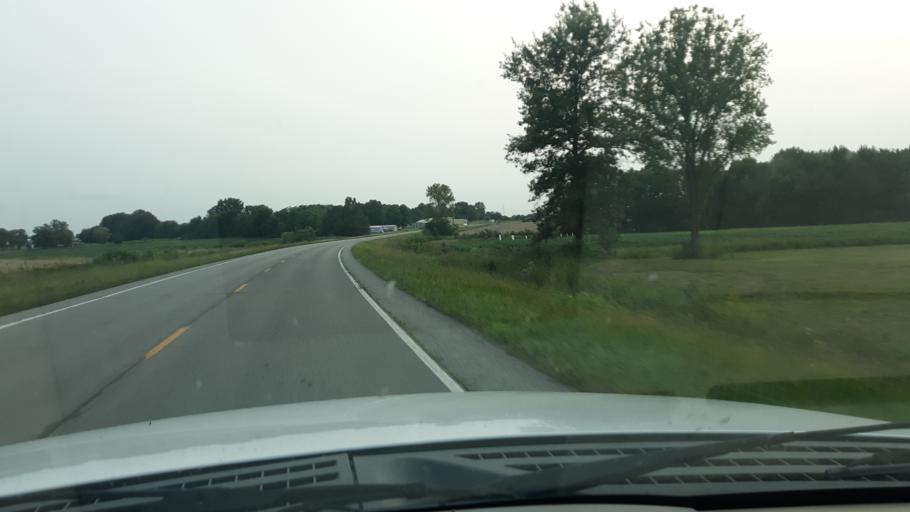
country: US
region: Illinois
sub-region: White County
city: Norris City
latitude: 37.9708
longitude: -88.3216
